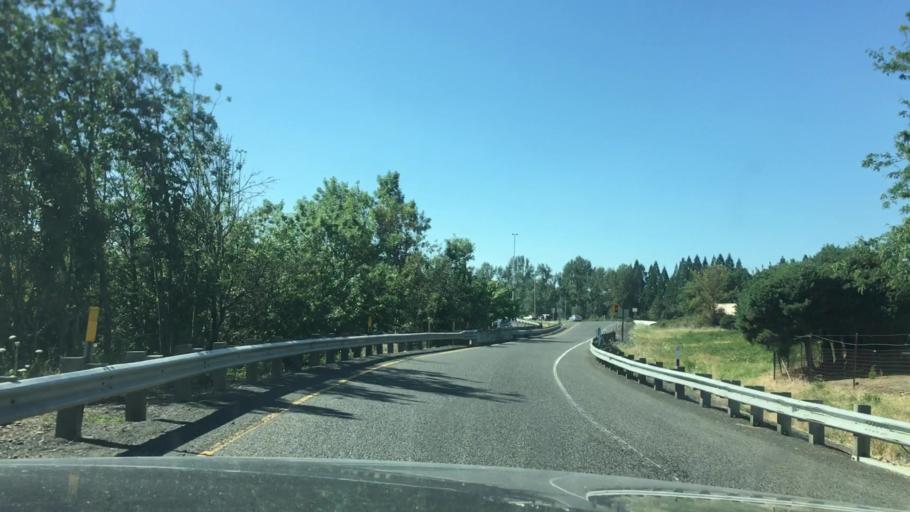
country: US
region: Oregon
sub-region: Lane County
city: Eugene
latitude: 44.0910
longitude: -123.0969
